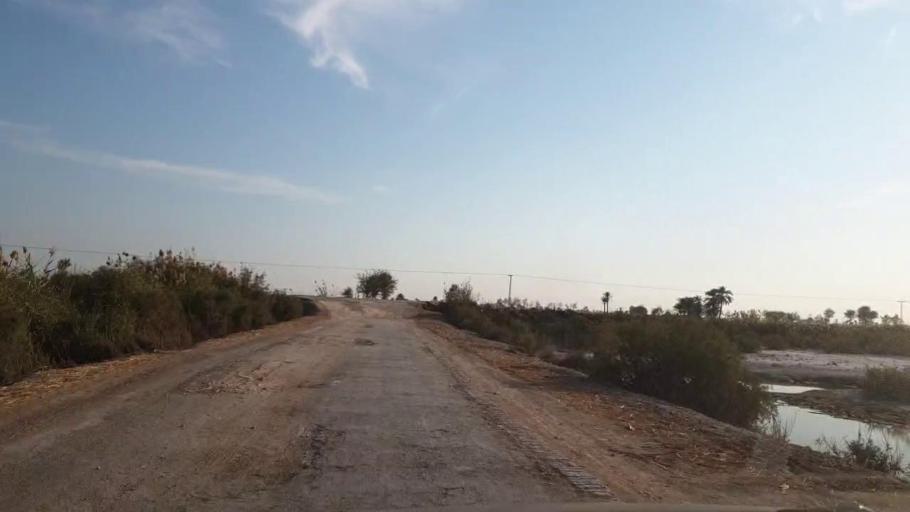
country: PK
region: Sindh
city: Khadro
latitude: 26.1788
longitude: 68.7501
